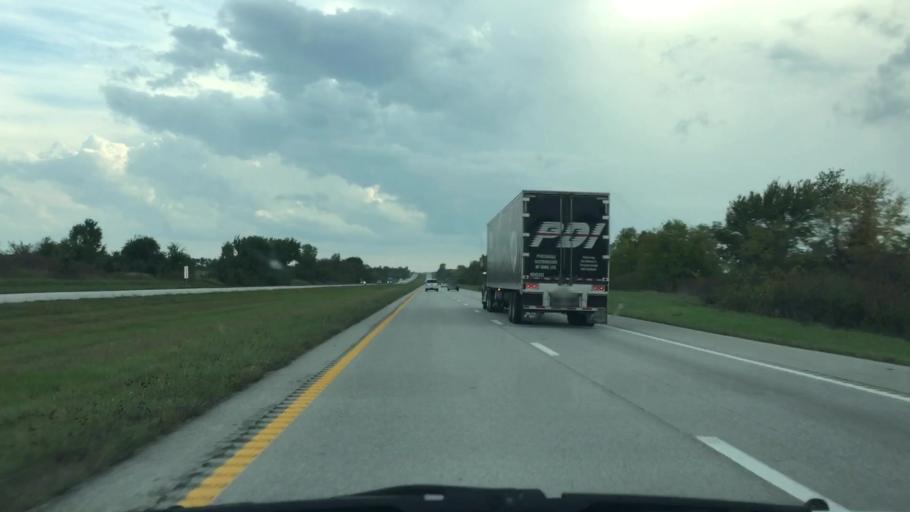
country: US
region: Missouri
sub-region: Clinton County
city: Cameron
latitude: 39.8285
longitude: -94.1880
